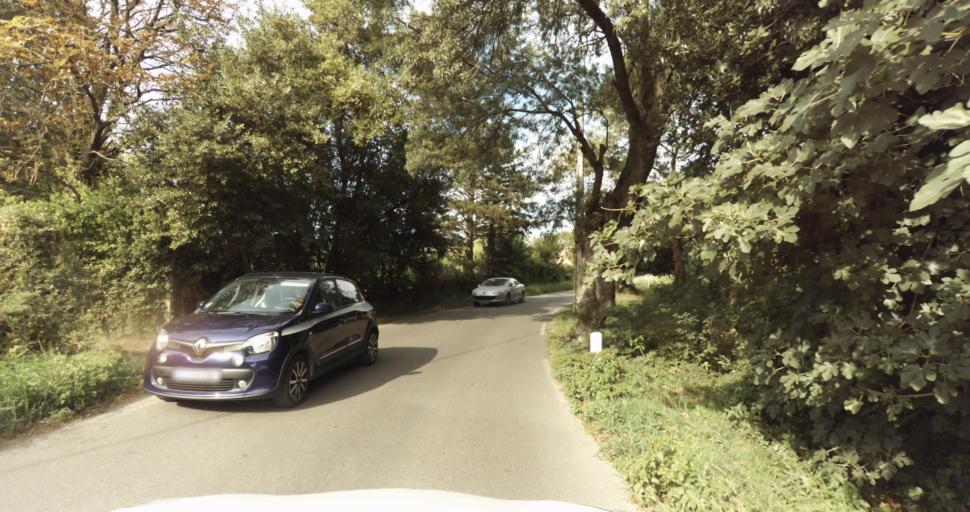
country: FR
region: Provence-Alpes-Cote d'Azur
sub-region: Departement des Bouches-du-Rhone
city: Miramas
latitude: 43.5727
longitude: 5.0197
